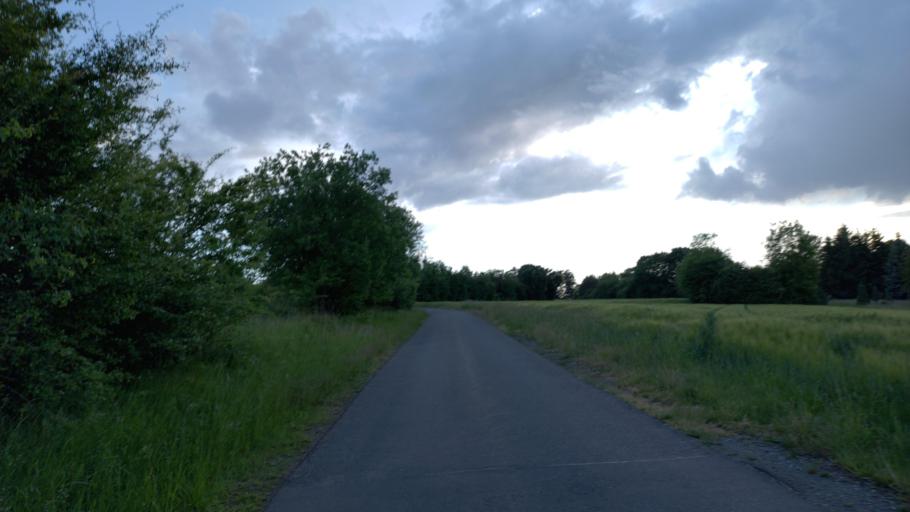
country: DE
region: Bavaria
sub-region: Upper Franconia
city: Bindlach
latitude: 50.0013
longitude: 11.6175
